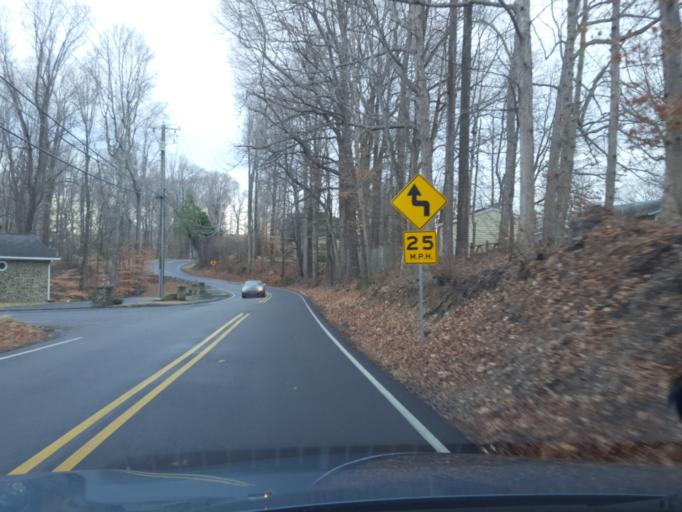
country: US
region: Maryland
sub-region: Calvert County
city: Chesapeake Beach
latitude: 38.6631
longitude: -76.5377
